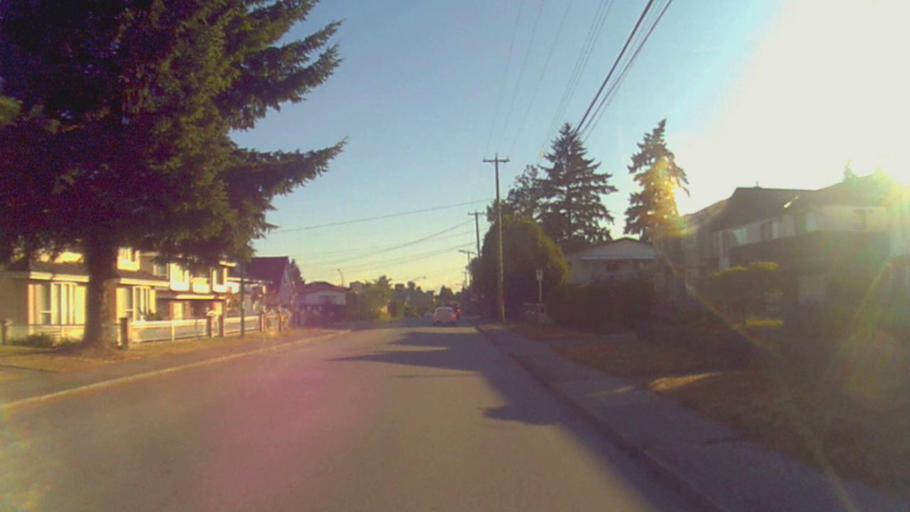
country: CA
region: British Columbia
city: New Westminster
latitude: 49.2226
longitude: -122.9257
